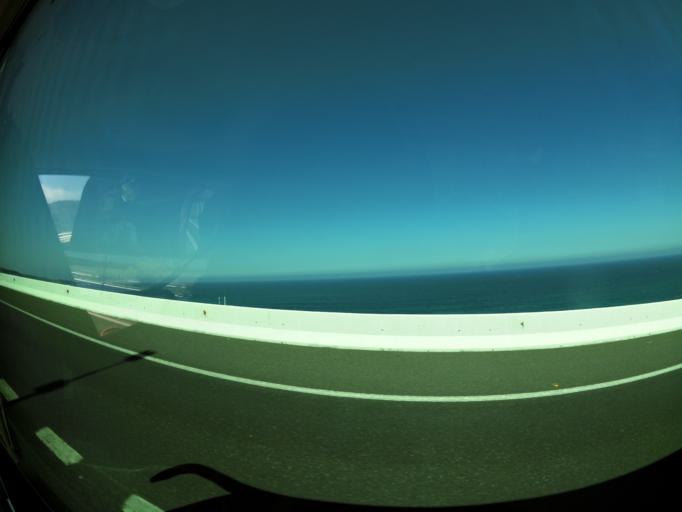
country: ES
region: Canary Islands
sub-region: Provincia de Las Palmas
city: Firgas
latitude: 28.1426
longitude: -15.5840
